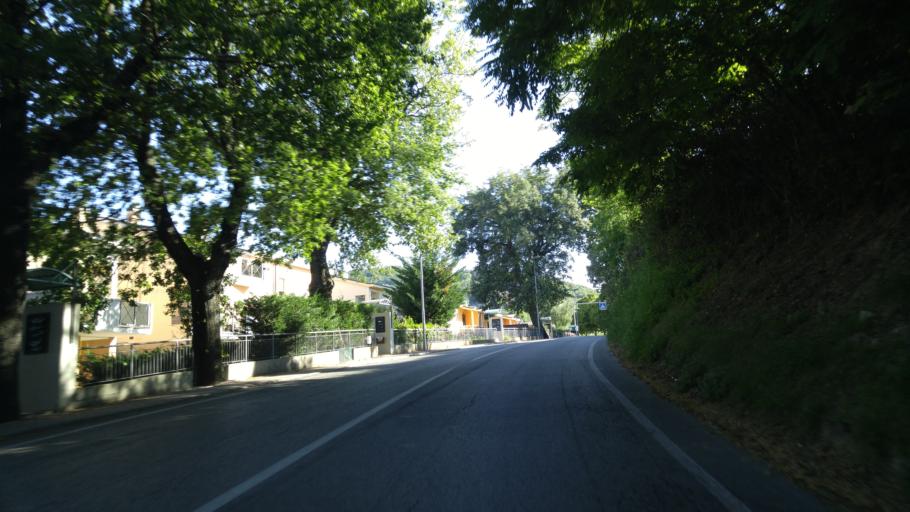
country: IT
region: The Marches
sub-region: Provincia di Pesaro e Urbino
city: Mombaroccio
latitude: 43.7993
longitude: 12.8673
